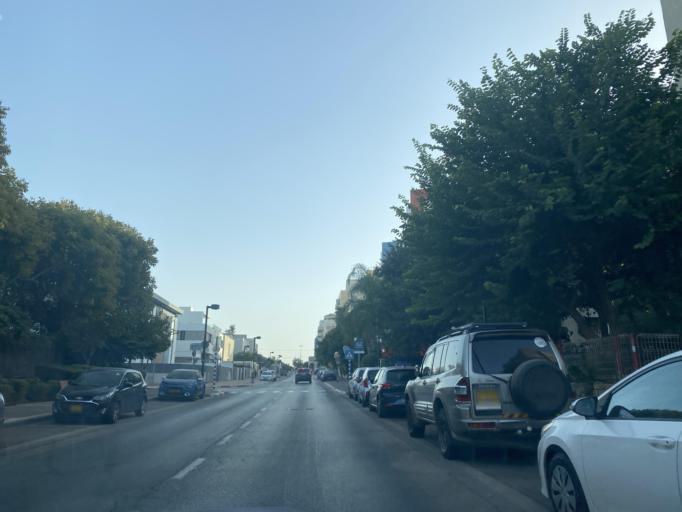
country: IL
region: Central District
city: Kfar Saba
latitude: 32.1616
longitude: 34.9067
